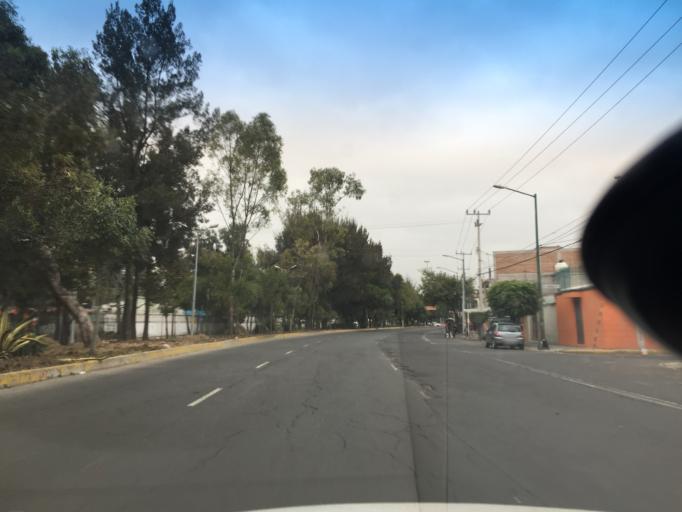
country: MX
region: Mexico City
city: Venustiano Carranza
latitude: 19.4669
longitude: -99.0777
